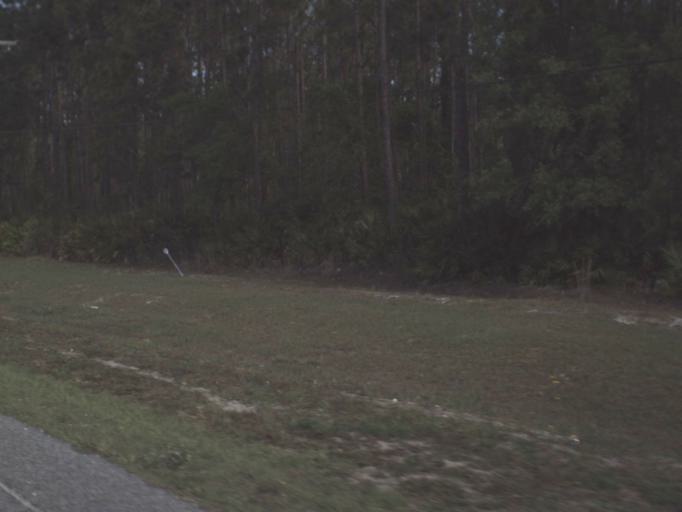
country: US
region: Florida
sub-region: Flagler County
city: Bunnell
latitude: 29.4279
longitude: -81.2238
